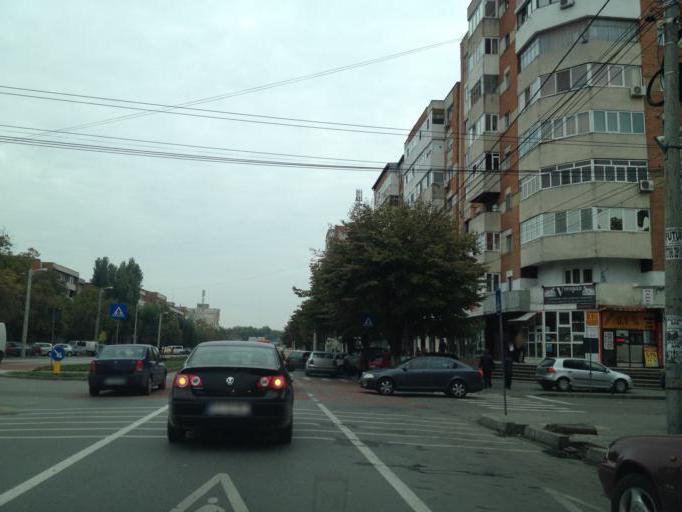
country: RO
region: Dolj
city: Craiova
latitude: 44.3046
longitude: 23.7954
